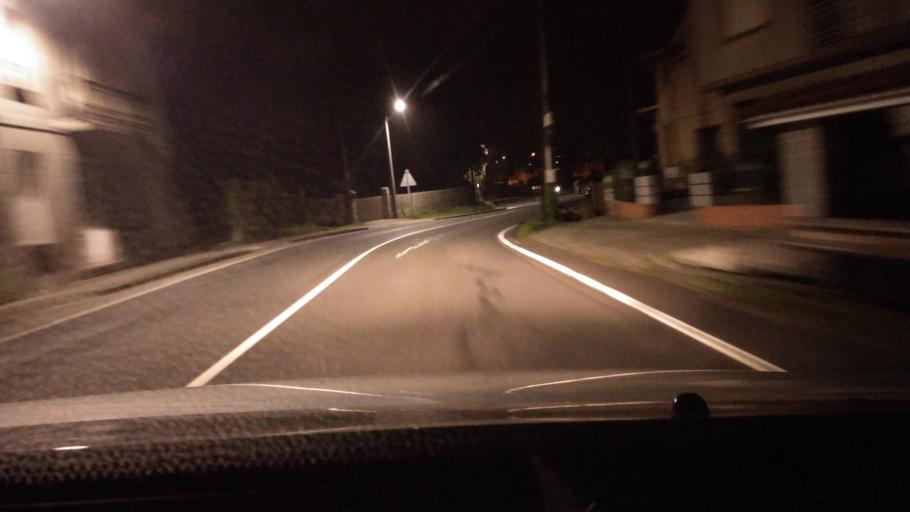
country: ES
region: Galicia
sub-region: Provincia de Pontevedra
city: Moana
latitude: 42.2769
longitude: -8.7480
